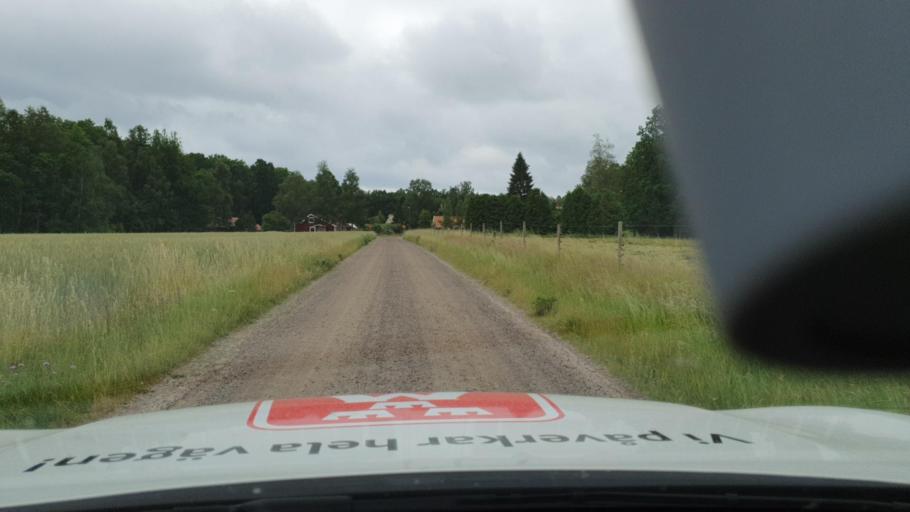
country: SE
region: Vaestra Goetaland
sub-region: Hjo Kommun
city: Hjo
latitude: 58.3566
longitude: 14.3366
